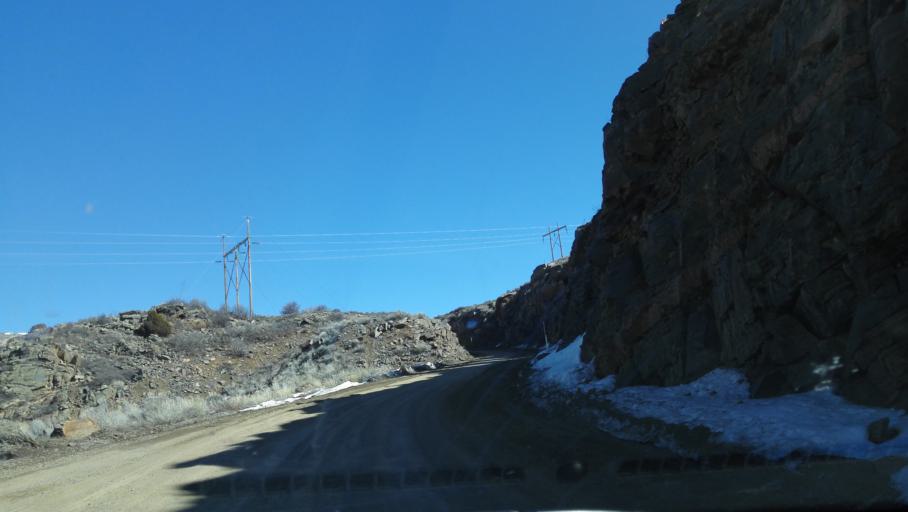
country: US
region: Colorado
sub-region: Hinsdale County
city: Lake City
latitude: 38.4453
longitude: -107.3433
